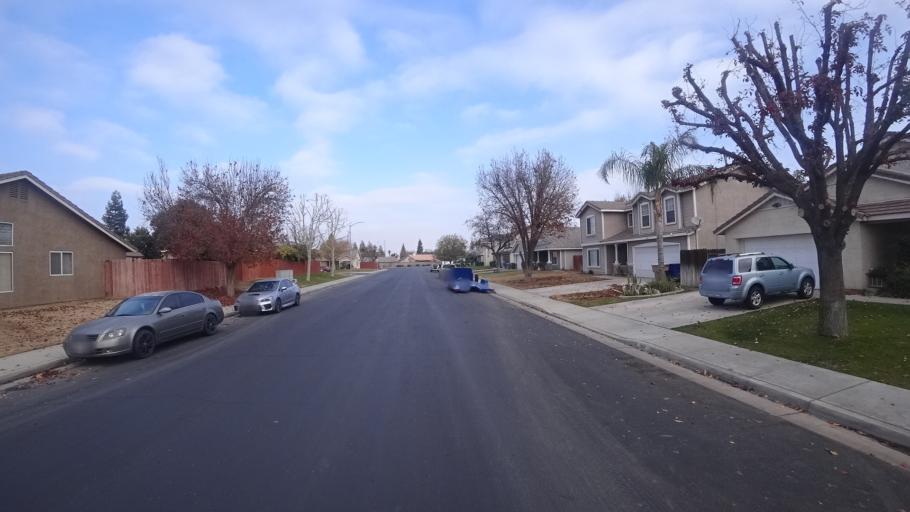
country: US
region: California
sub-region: Kern County
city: Greenfield
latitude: 35.3022
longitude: -119.0680
